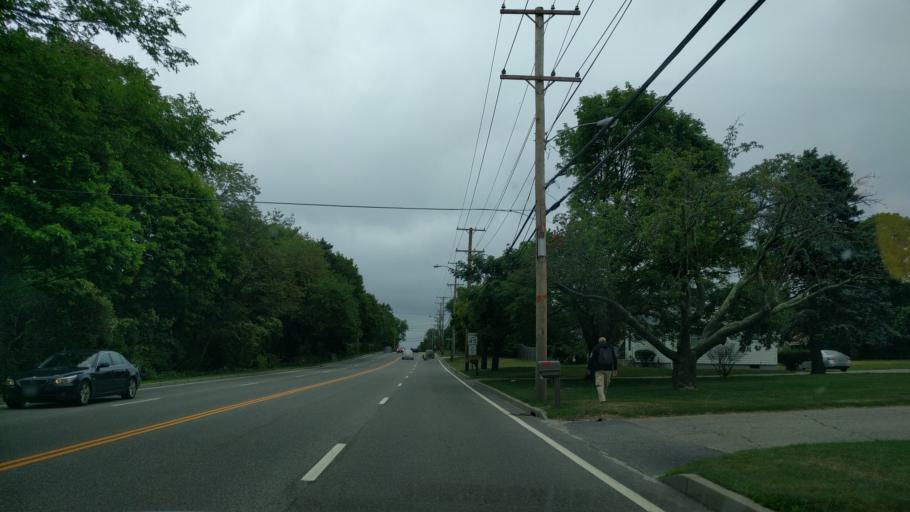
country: US
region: Rhode Island
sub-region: Newport County
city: Melville
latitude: 41.5836
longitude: -71.2694
